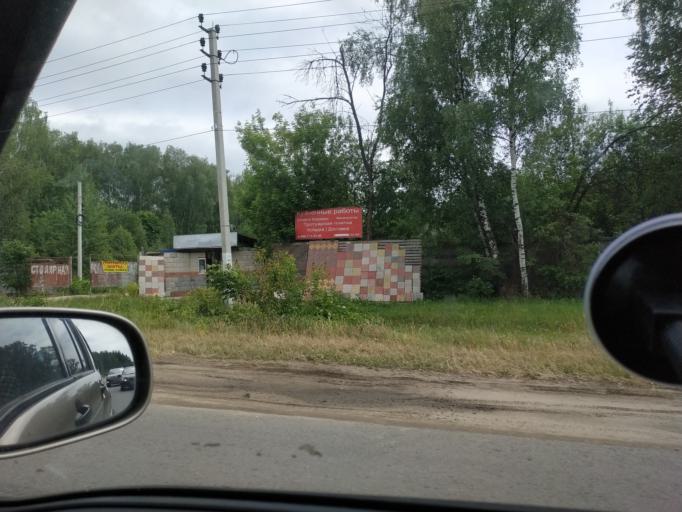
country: RU
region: Moskovskaya
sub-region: Shchelkovskiy Rayon
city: Grebnevo
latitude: 55.9712
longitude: 38.0890
